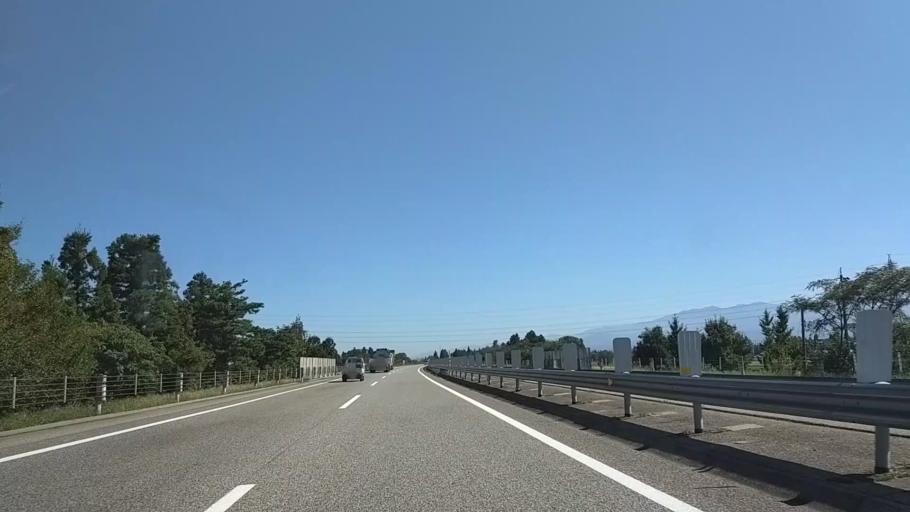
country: JP
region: Toyama
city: Toyama-shi
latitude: 36.6596
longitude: 137.2604
